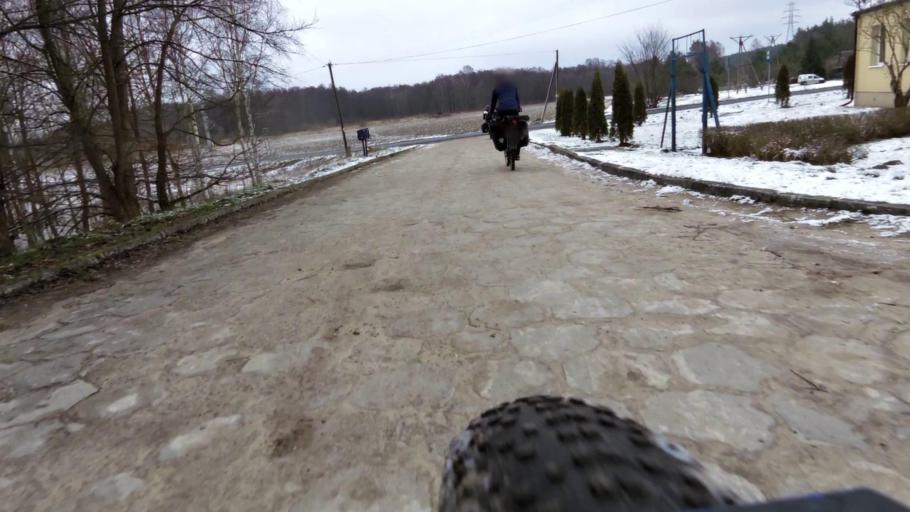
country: PL
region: West Pomeranian Voivodeship
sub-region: Powiat walecki
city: Miroslawiec
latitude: 53.3341
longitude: 16.1027
